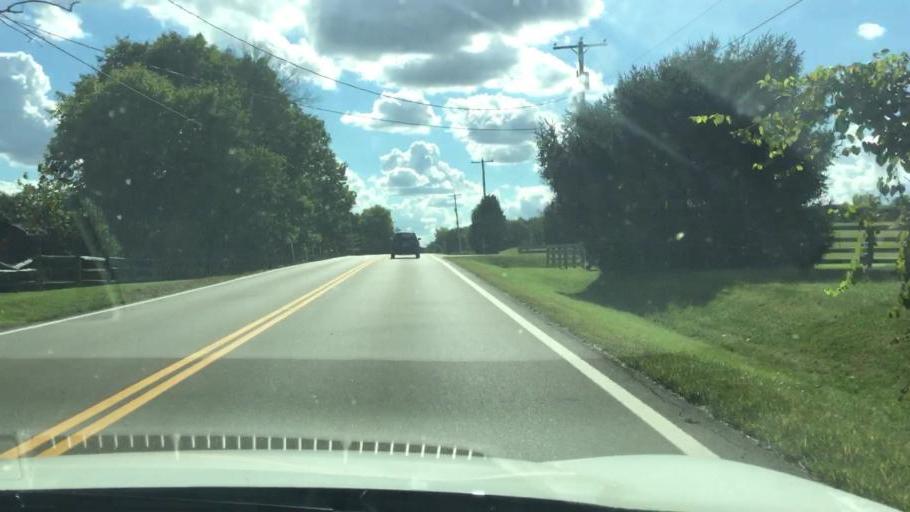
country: US
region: Ohio
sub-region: Clark County
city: Northridge
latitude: 39.9795
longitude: -83.7416
